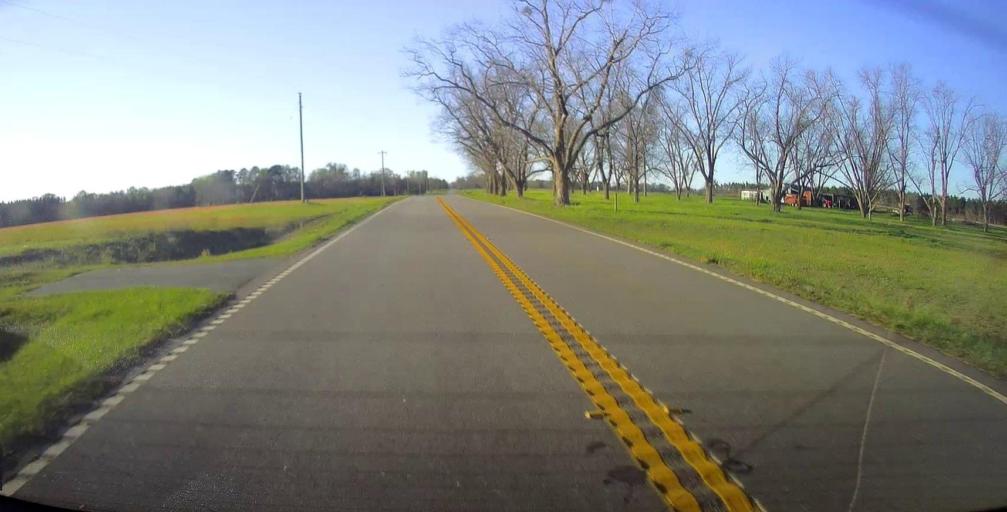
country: US
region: Georgia
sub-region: Wilcox County
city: Abbeville
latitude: 32.1461
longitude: -83.3464
